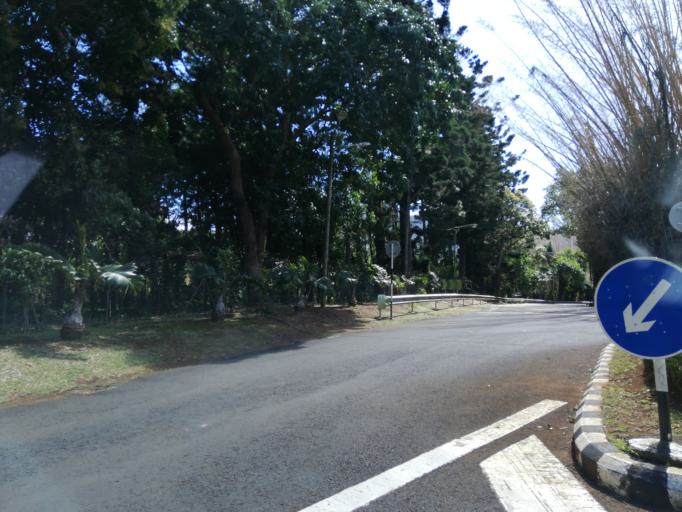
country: MU
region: Moka
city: Moka
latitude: -20.2305
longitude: 57.4959
